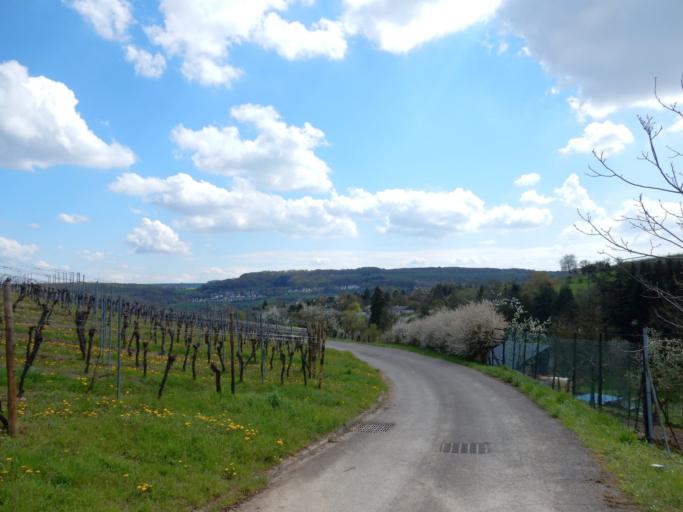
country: LU
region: Grevenmacher
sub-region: Canton de Grevenmacher
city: Grevenmacher
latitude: 49.6843
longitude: 6.4312
